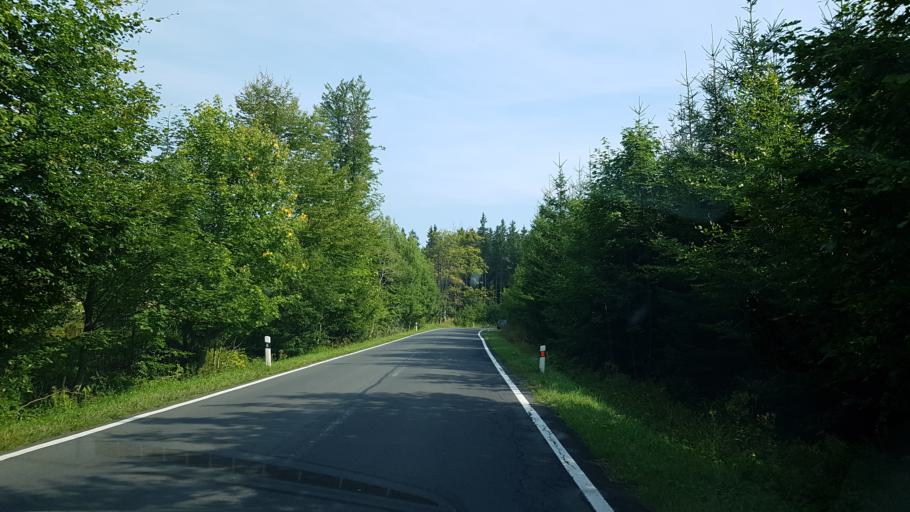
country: CZ
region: Olomoucky
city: Pisecna
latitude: 50.2236
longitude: 17.2735
